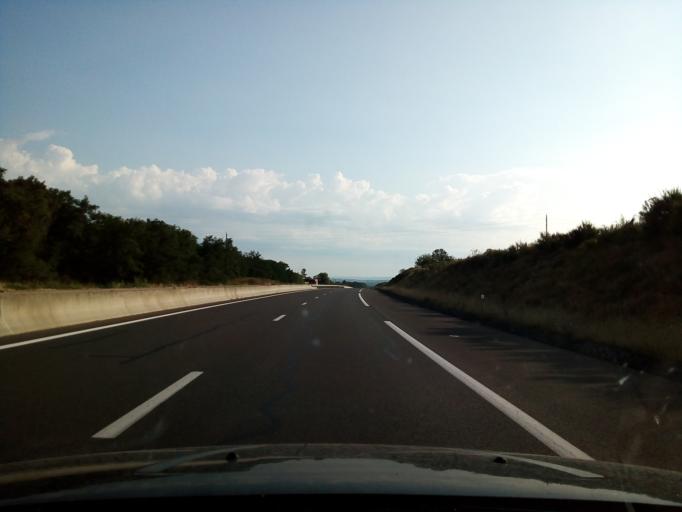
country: FR
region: Auvergne
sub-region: Departement de l'Allier
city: Quinssaines
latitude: 46.3393
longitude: 2.5365
